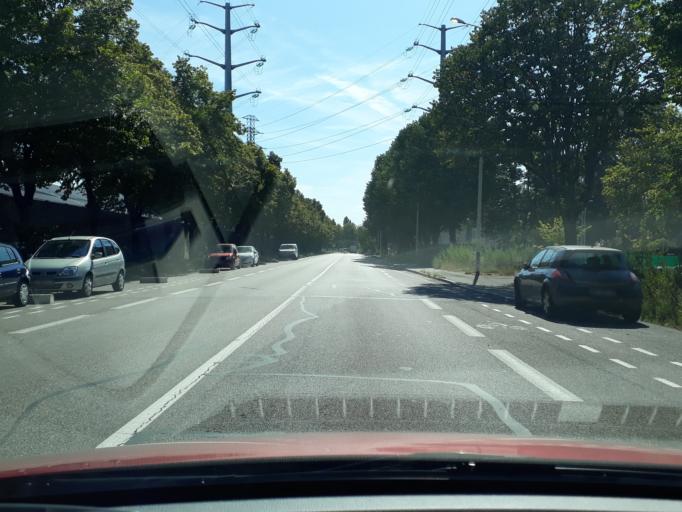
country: FR
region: Rhone-Alpes
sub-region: Departement du Rhone
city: Venissieux
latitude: 45.7034
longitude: 4.9026
